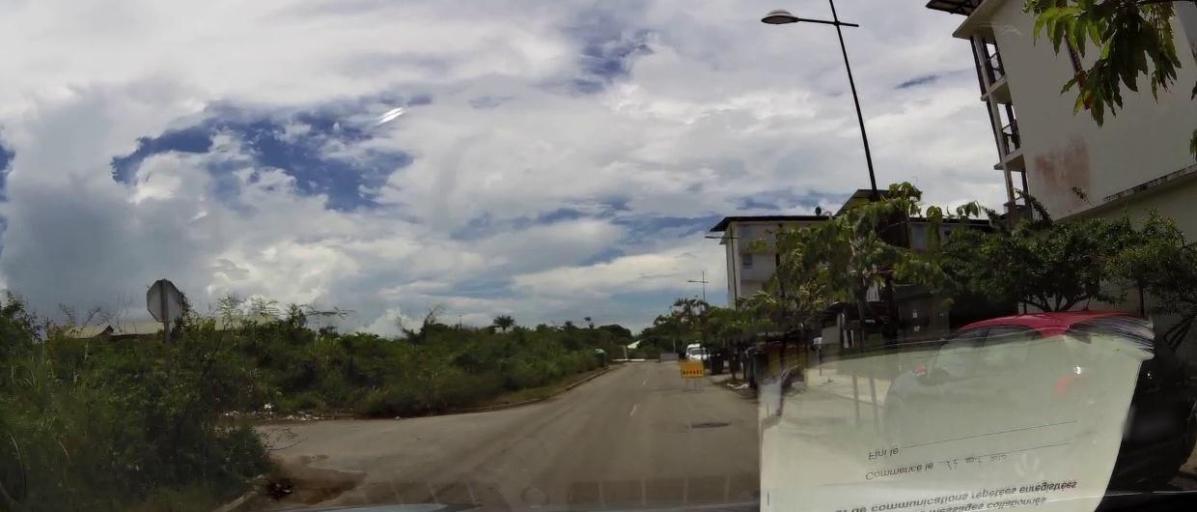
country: GF
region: Guyane
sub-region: Guyane
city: Cayenne
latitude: 4.9345
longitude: -52.3027
